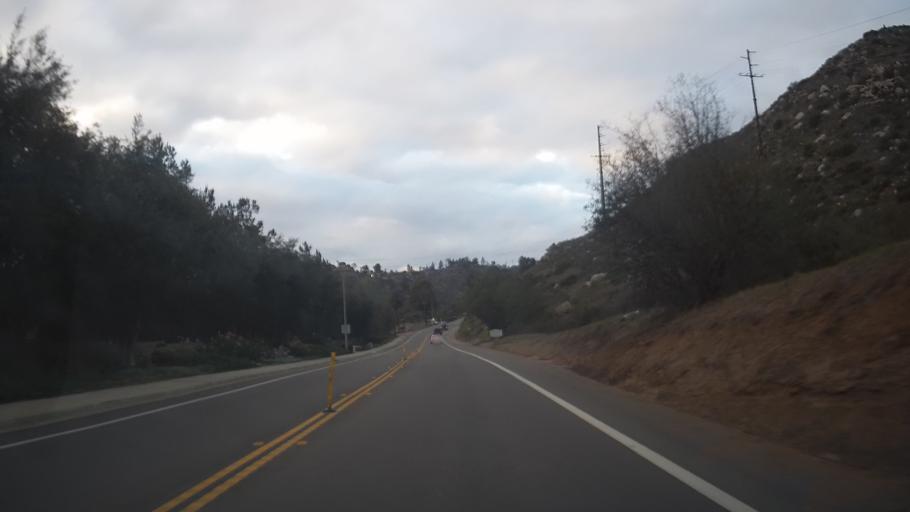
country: US
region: California
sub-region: San Diego County
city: Crest
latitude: 32.7842
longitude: -116.8800
